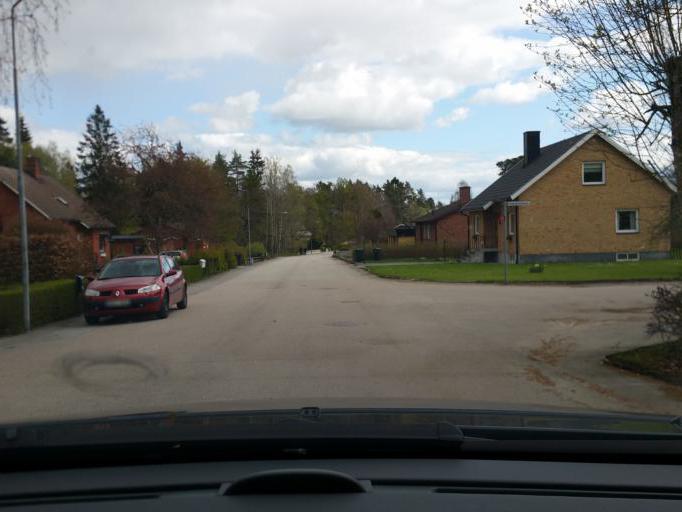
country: SE
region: Kronoberg
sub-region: Vaxjo Kommun
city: Lammhult
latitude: 57.1735
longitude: 14.5729
